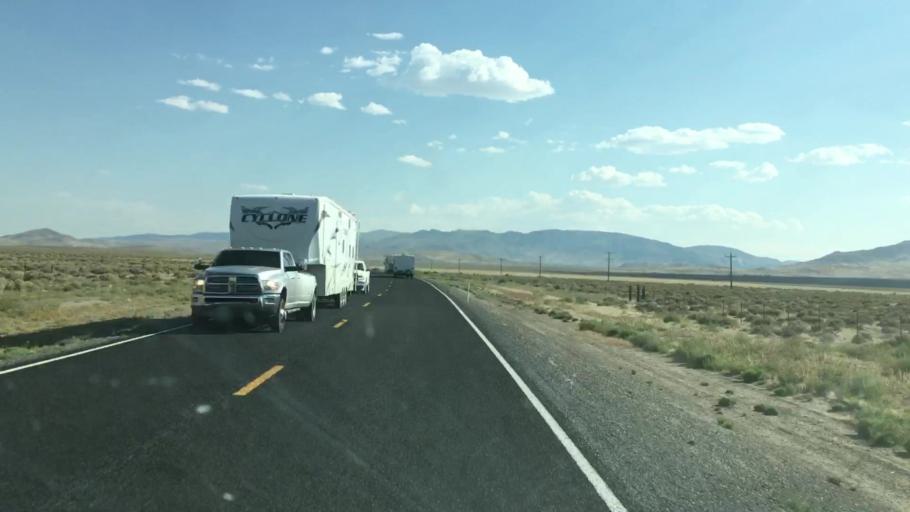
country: US
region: Nevada
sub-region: Lyon County
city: Fernley
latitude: 39.6864
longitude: -119.3353
